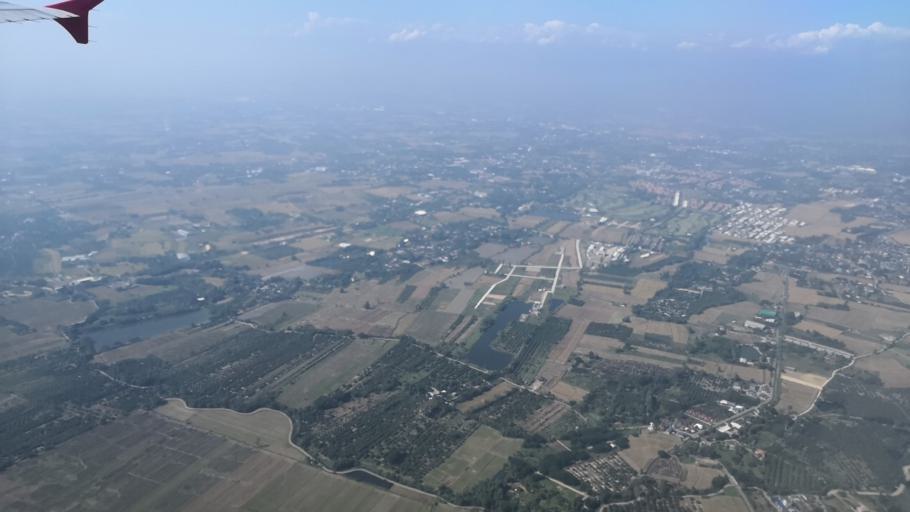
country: TH
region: Chiang Mai
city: Saraphi
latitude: 18.6993
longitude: 98.9903
